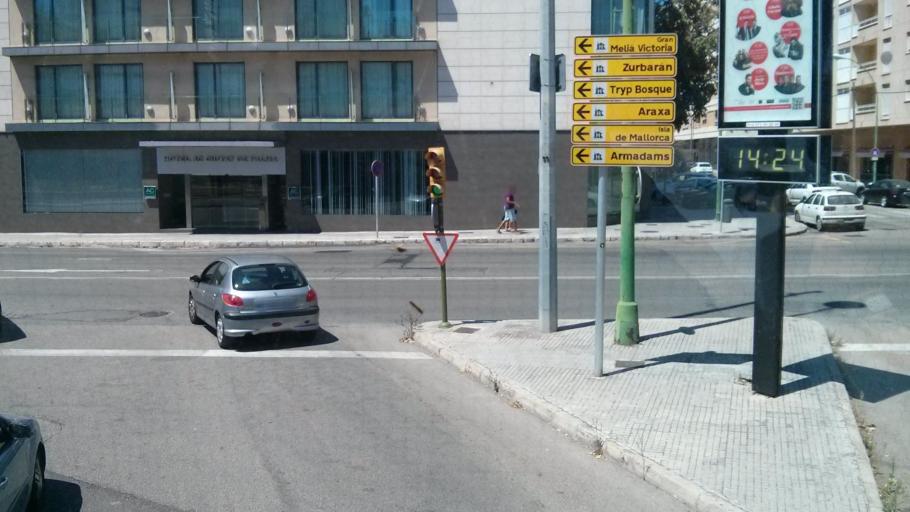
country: ES
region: Balearic Islands
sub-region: Illes Balears
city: Palma
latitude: 39.5701
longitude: 2.6335
